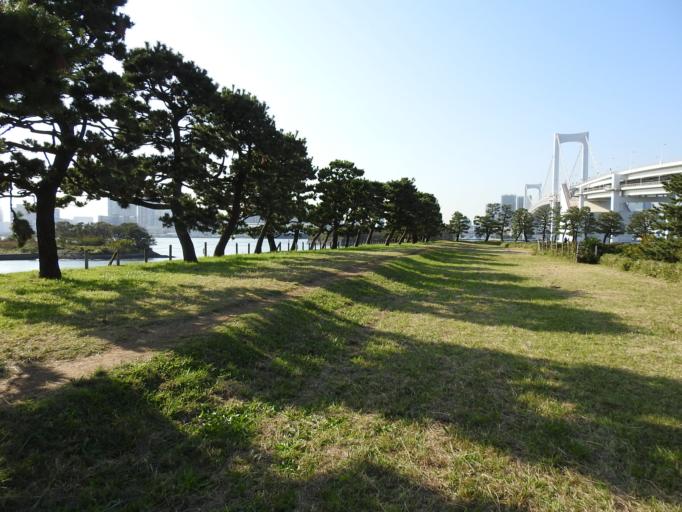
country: JP
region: Tokyo
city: Tokyo
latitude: 35.6329
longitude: 139.7722
